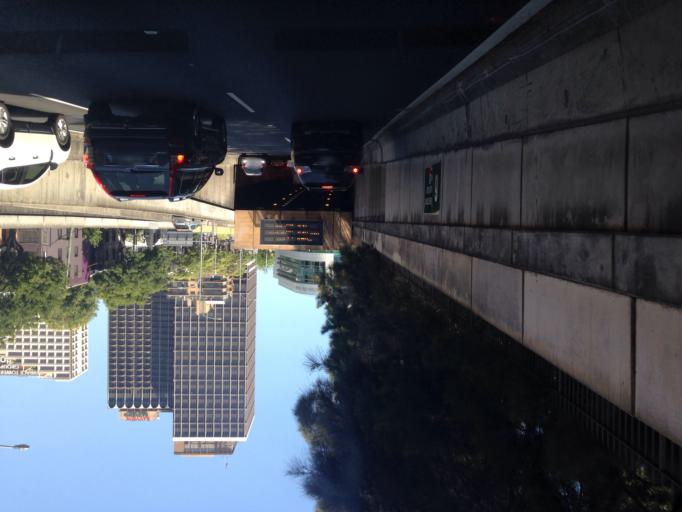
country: AU
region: New South Wales
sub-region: City of Sydney
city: Darlinghurst
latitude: -33.8714
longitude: 151.2182
